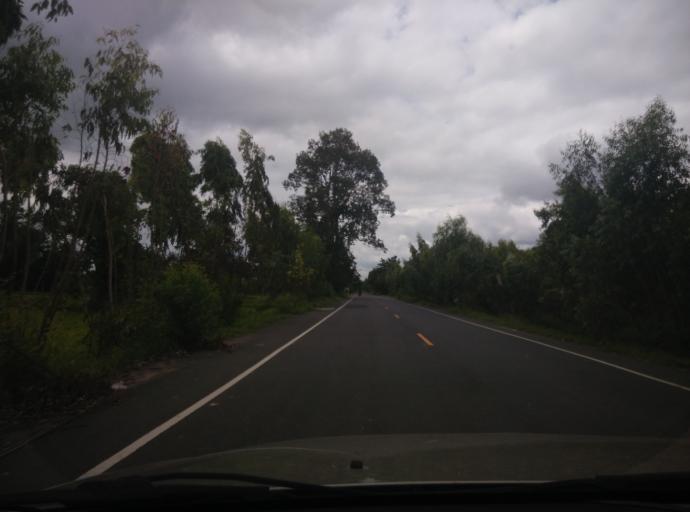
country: TH
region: Sisaket
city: Uthumphon Phisai
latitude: 15.1312
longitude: 104.1541
